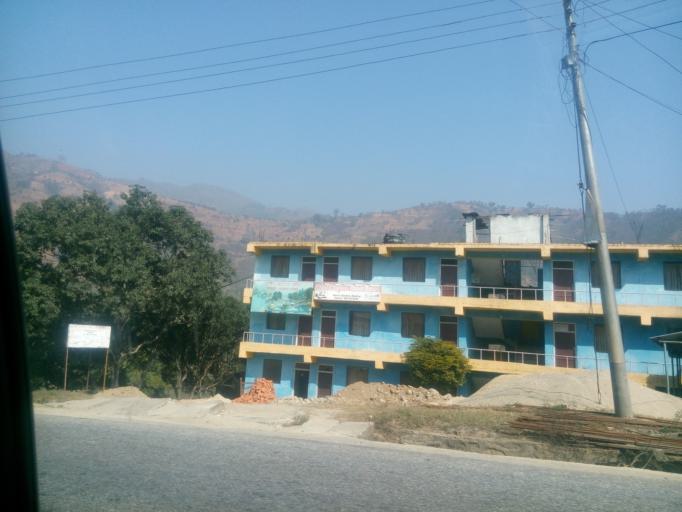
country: NP
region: Central Region
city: Kirtipur
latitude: 27.8049
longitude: 84.9057
